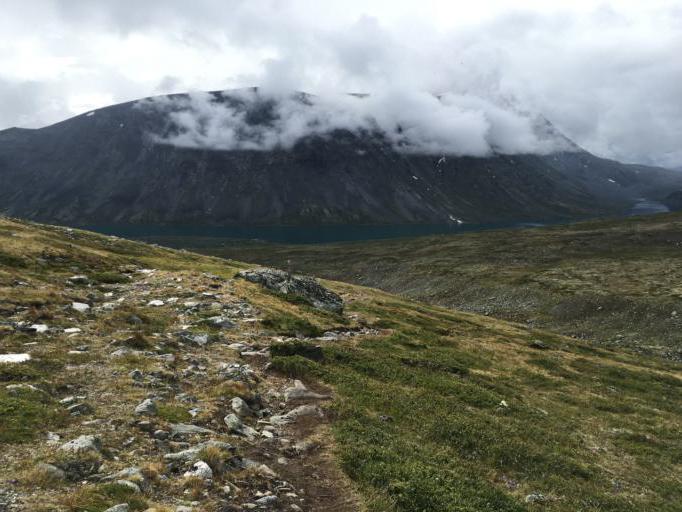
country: NO
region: Oppland
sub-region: Lom
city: Fossbergom
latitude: 61.5723
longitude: 8.6730
